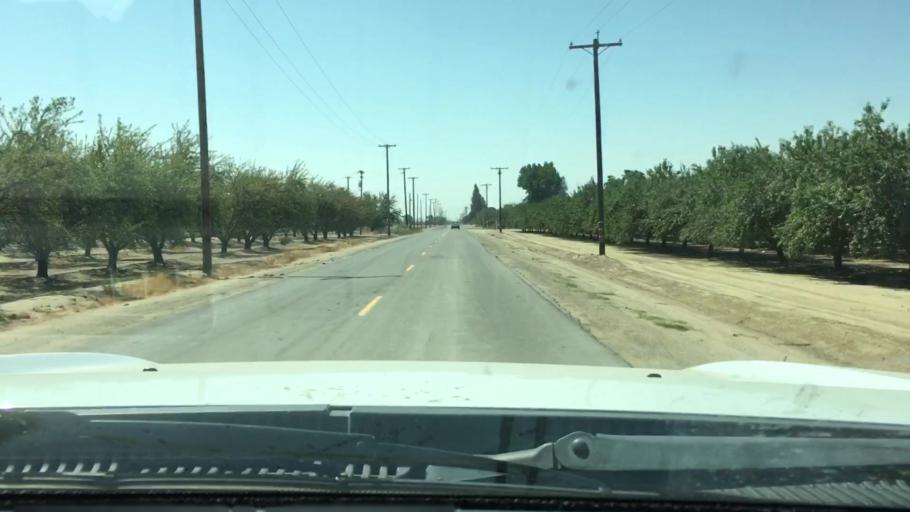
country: US
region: California
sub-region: Kern County
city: Shafter
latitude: 35.5382
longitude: -119.2778
